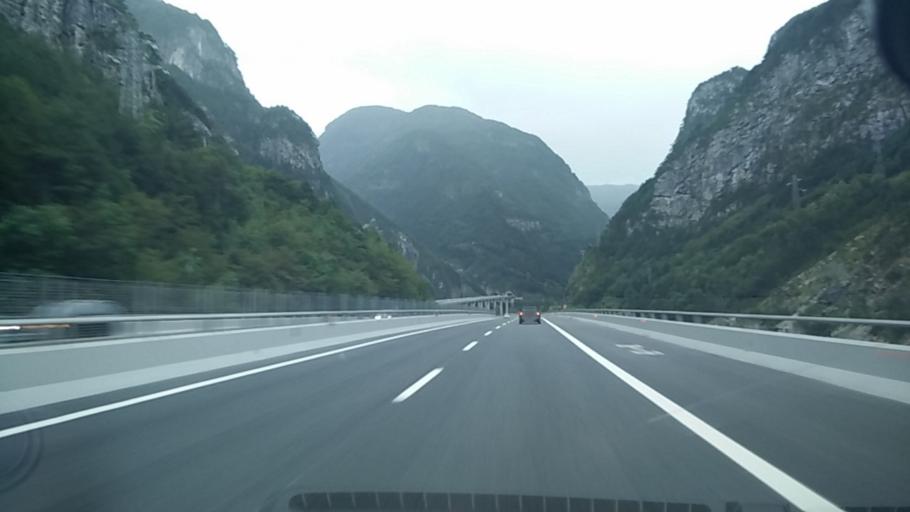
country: IT
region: Friuli Venezia Giulia
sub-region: Provincia di Udine
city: Dogna
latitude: 46.4306
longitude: 13.3153
